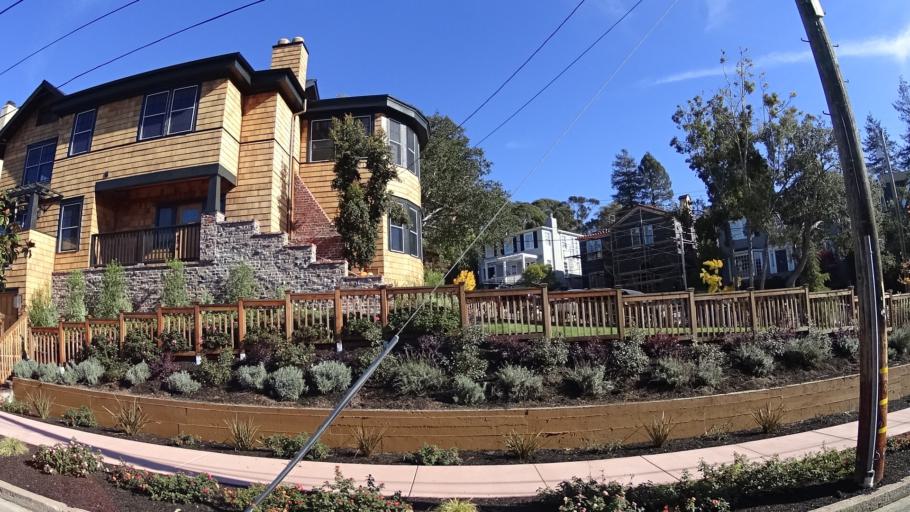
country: US
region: California
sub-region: Alameda County
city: Piedmont
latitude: 37.8282
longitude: -122.2403
